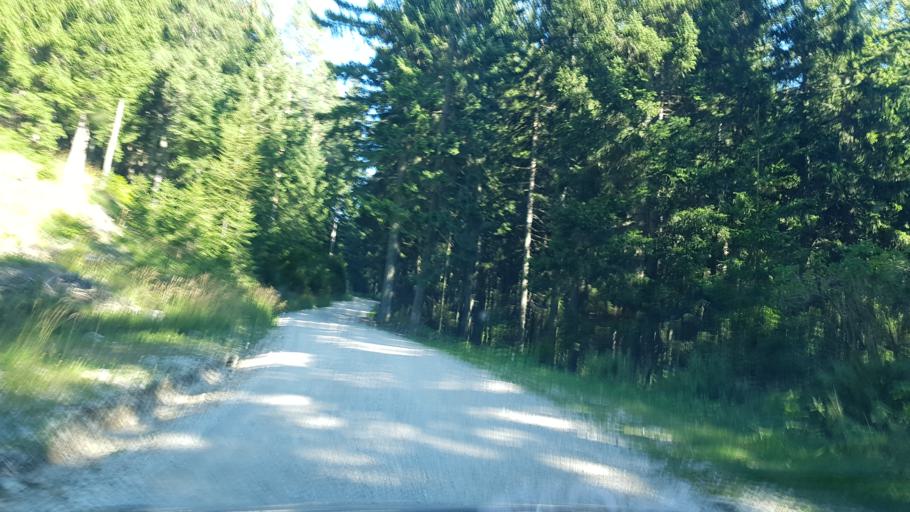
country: SI
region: Ravne na Koroskem
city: Kotlje
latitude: 46.4784
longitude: 14.9566
